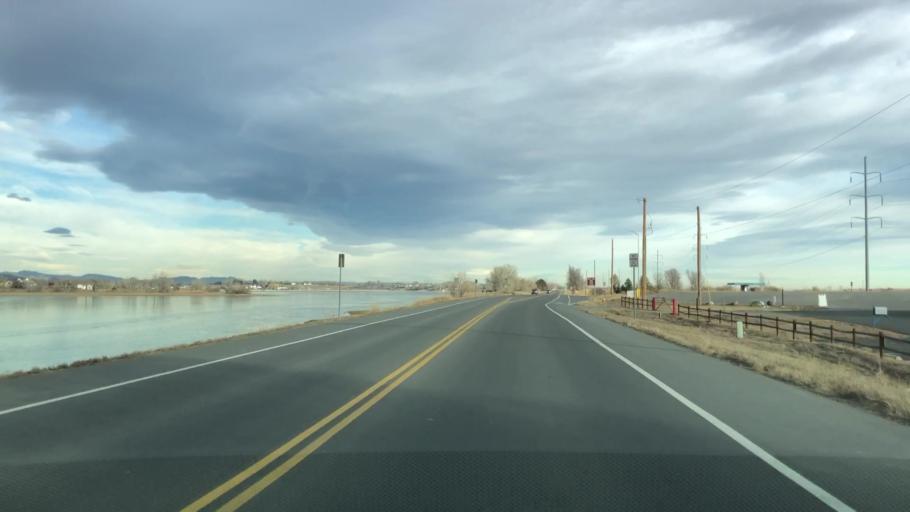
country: US
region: Colorado
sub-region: Larimer County
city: Loveland
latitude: 40.4298
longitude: -105.0454
